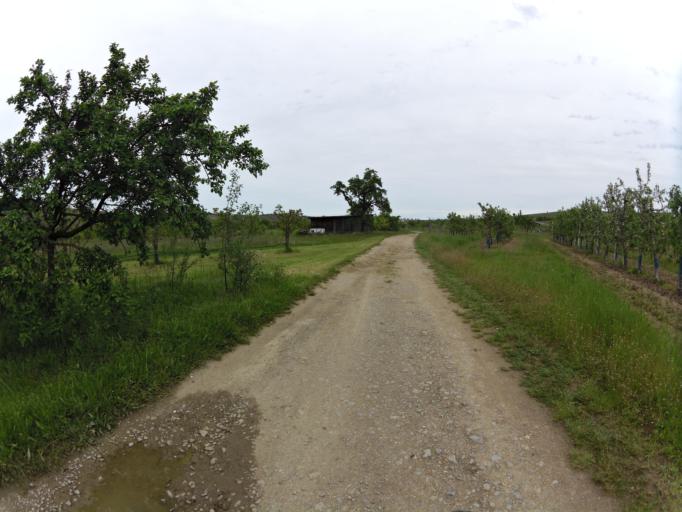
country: DE
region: Bavaria
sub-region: Regierungsbezirk Unterfranken
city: Nordheim
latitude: 49.8483
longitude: 10.1710
